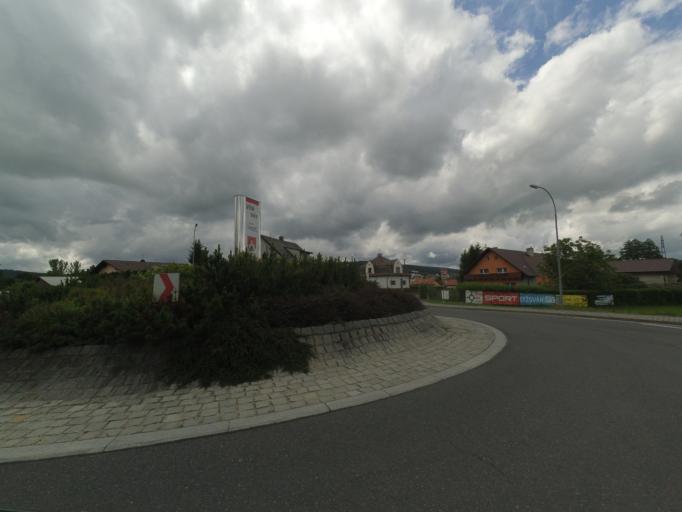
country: CZ
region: Plzensky
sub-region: Okres Klatovy
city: Nyrsko
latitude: 49.2961
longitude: 13.1503
